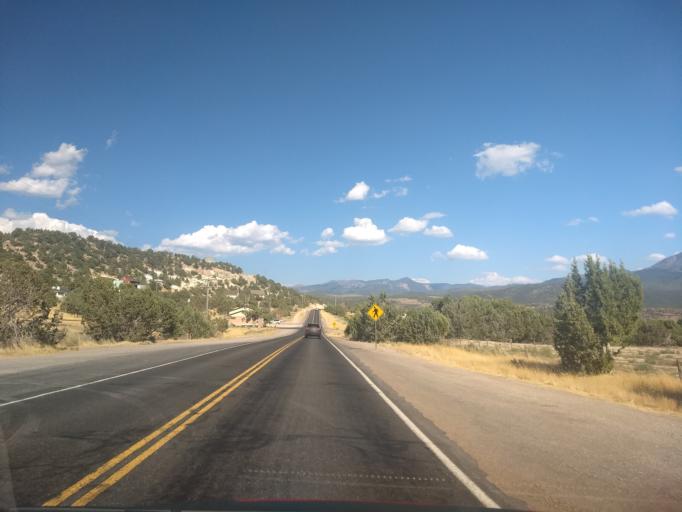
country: US
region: Utah
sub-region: Washington County
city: Enterprise
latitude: 37.4170
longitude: -113.6311
